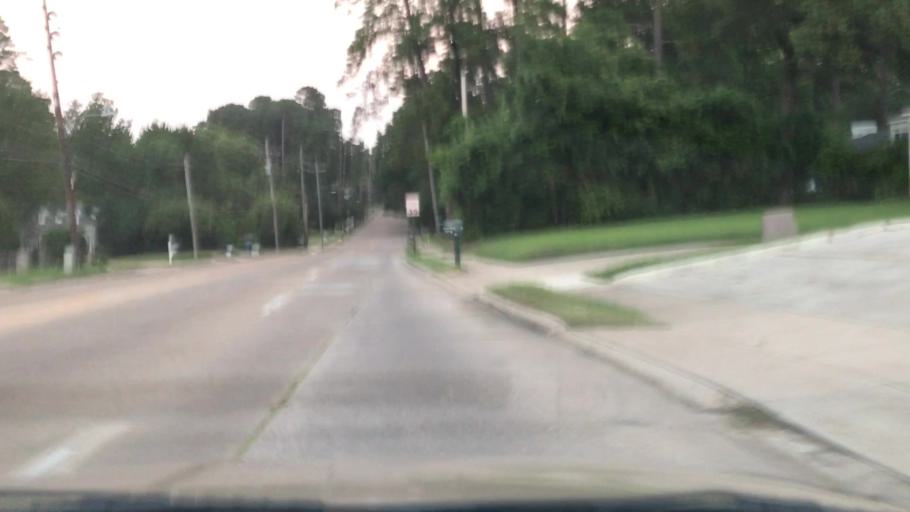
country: US
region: Louisiana
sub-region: Bossier Parish
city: Bossier City
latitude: 32.4546
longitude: -93.7452
